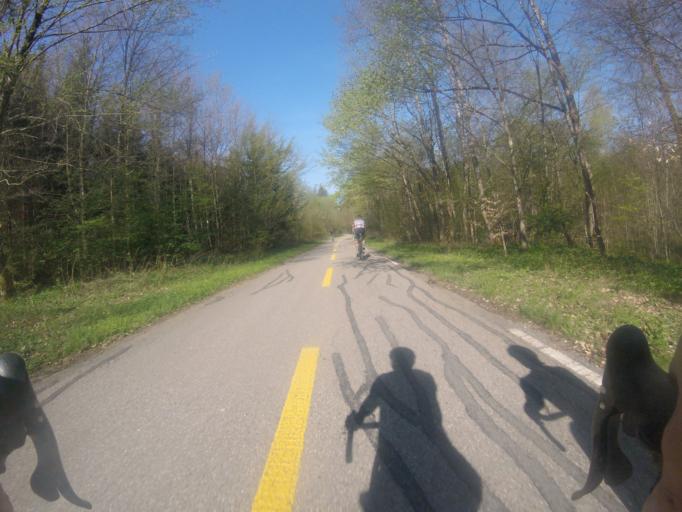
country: CH
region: Bern
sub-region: Bern-Mittelland District
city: Wohlen
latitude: 46.9641
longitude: 7.3953
